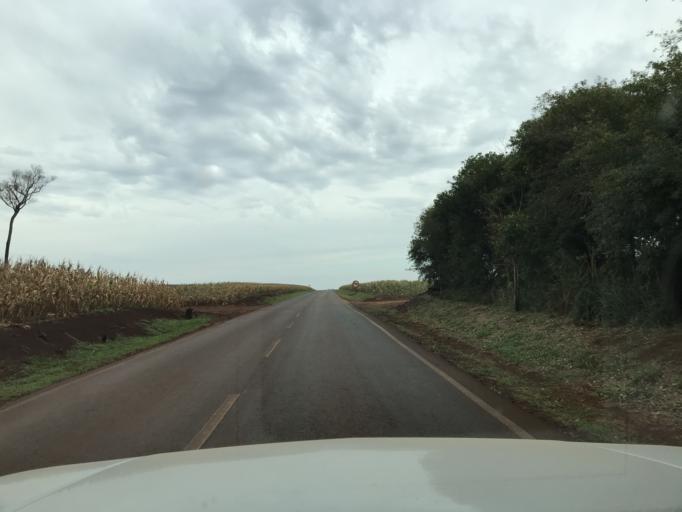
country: BR
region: Parana
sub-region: Palotina
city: Palotina
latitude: -24.4386
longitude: -53.9150
